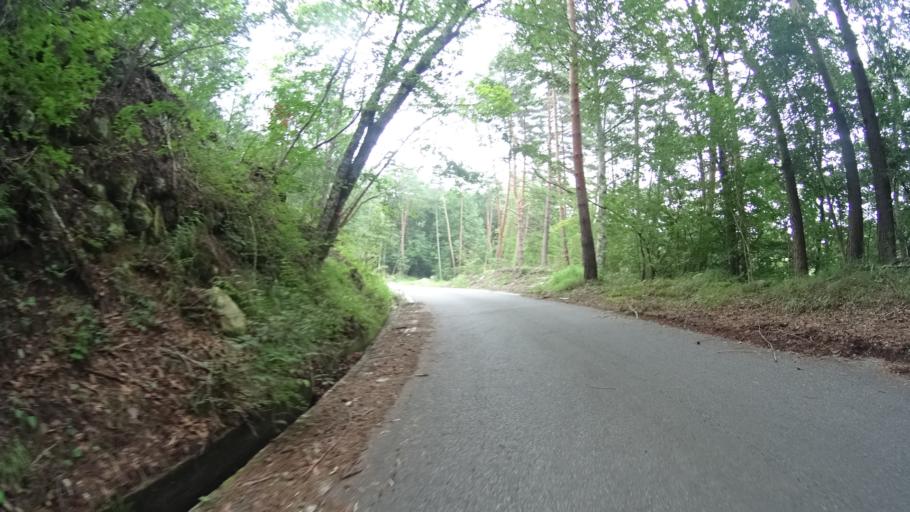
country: JP
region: Yamanashi
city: Kofu-shi
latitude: 35.8050
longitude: 138.5885
